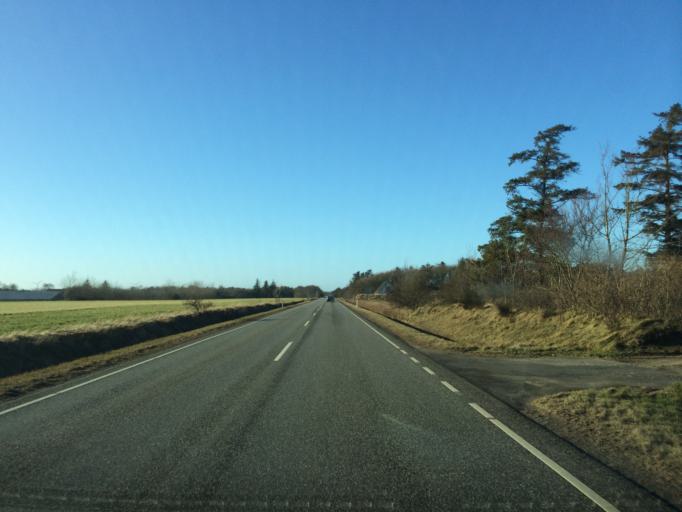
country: DK
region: Central Jutland
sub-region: Ringkobing-Skjern Kommune
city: Ringkobing
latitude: 56.1154
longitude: 8.3045
